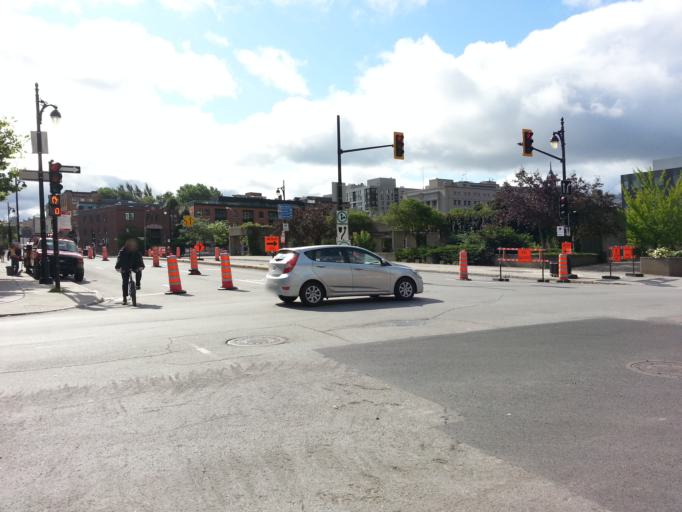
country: CA
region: Quebec
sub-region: Montreal
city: Montreal
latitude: 45.5126
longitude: -73.5549
